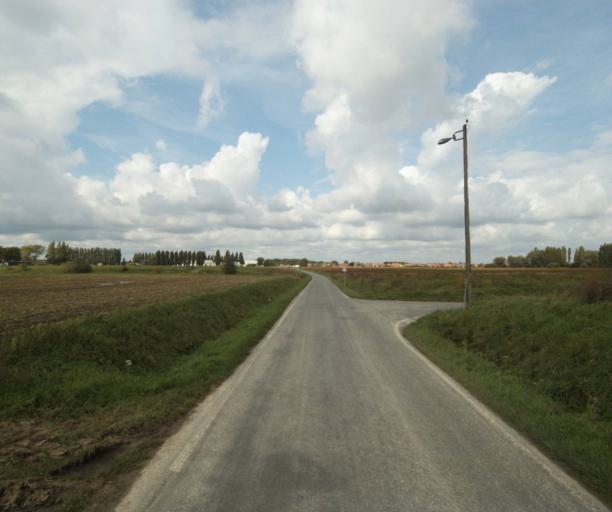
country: FR
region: Nord-Pas-de-Calais
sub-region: Departement du Nord
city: Houplines
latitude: 50.6853
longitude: 2.9265
